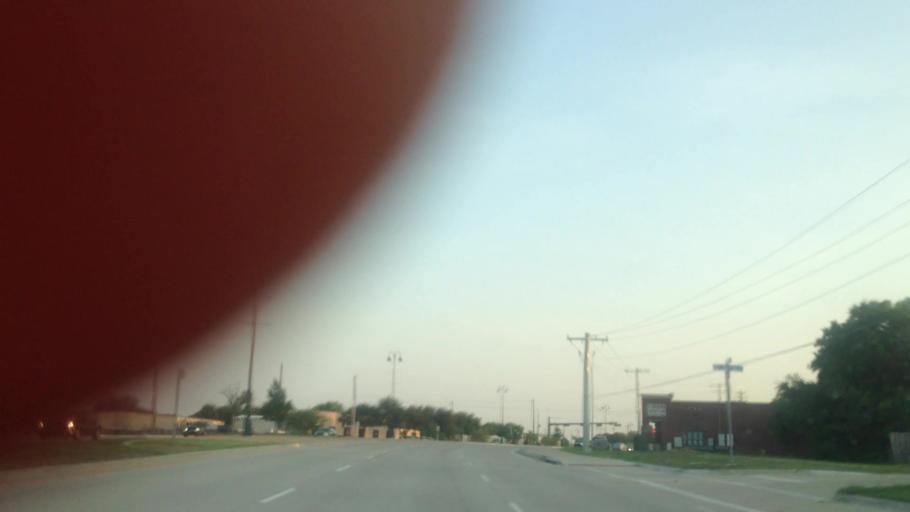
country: US
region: Texas
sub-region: Denton County
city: The Colony
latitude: 33.1056
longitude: -96.8920
